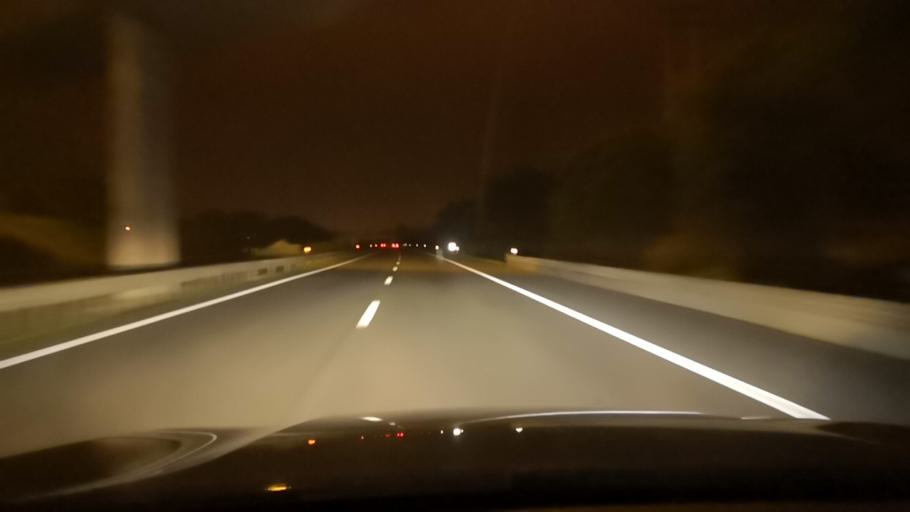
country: PT
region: Setubal
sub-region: Palmela
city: Palmela
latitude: 38.5567
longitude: -8.8697
